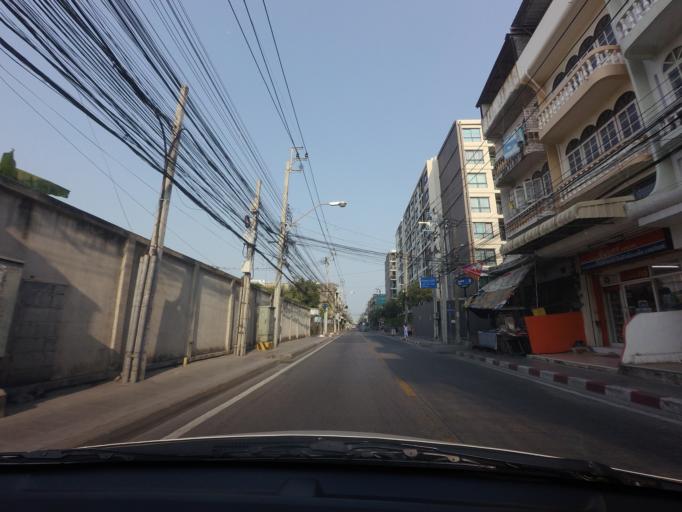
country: TH
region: Bangkok
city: Bang Na
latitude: 13.6616
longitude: 100.6053
